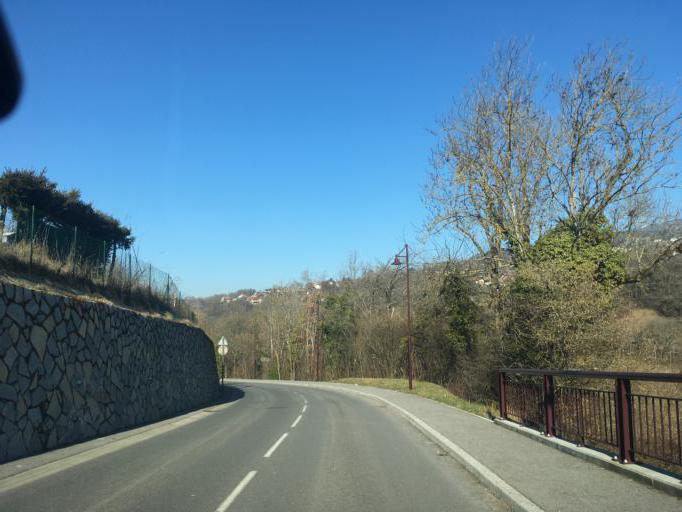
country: FR
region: Rhone-Alpes
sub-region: Departement de la Haute-Savoie
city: Cranves-Sales
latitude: 46.1884
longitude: 6.2929
